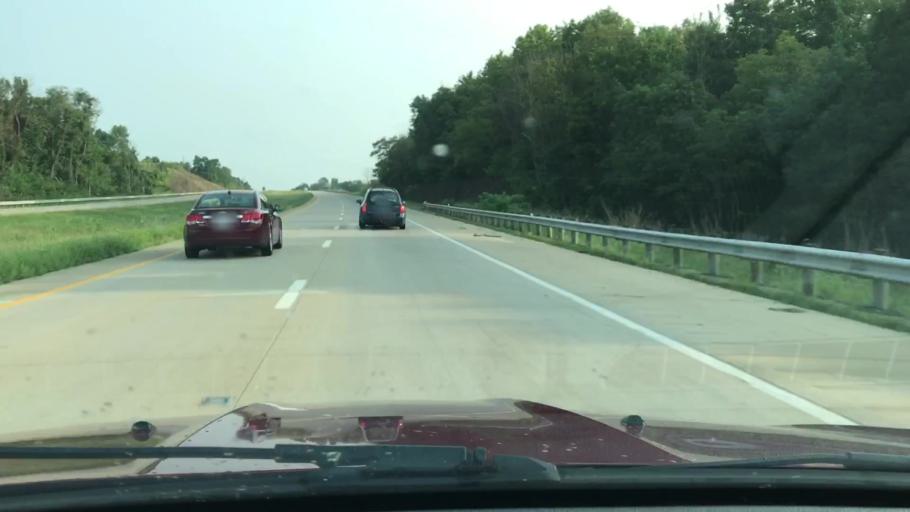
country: US
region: Ohio
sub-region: Washington County
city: Devola
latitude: 39.5506
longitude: -81.4479
